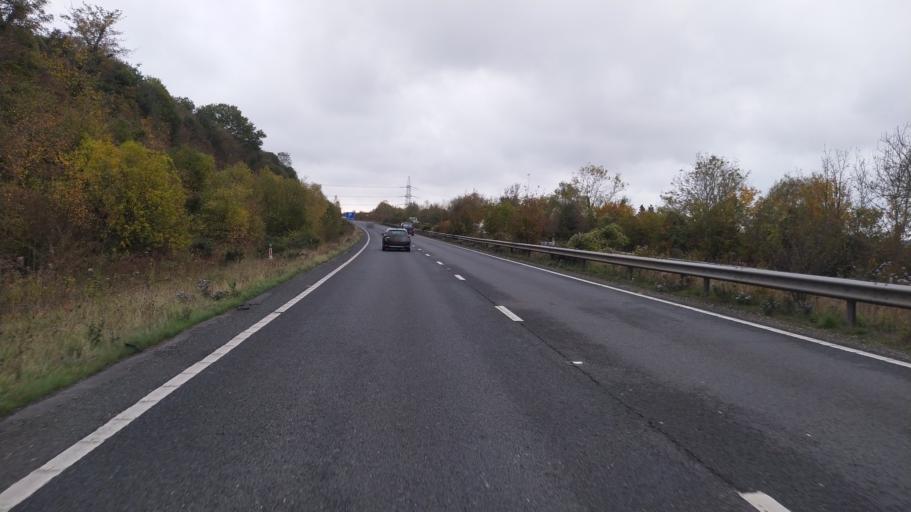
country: GB
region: England
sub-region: Hampshire
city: Cowplain
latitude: 50.9374
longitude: -0.9914
